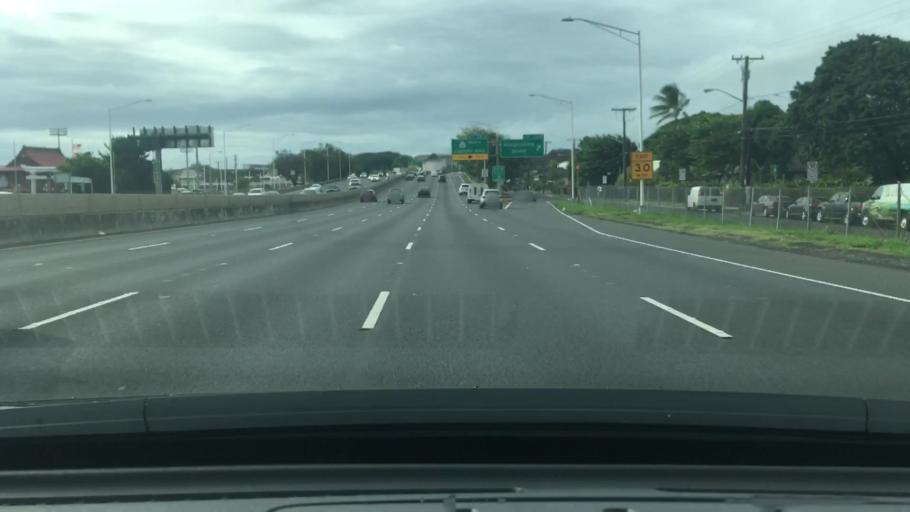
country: US
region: Hawaii
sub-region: Honolulu County
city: Honolulu
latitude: 21.3278
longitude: -157.8682
